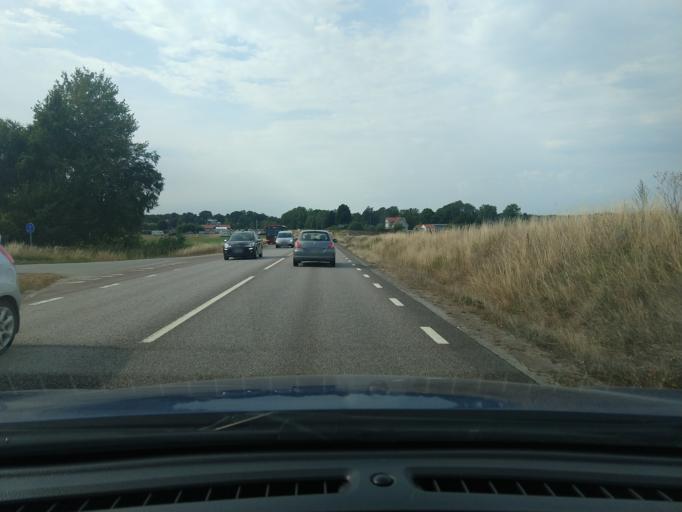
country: SE
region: Blekinge
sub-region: Karlskrona Kommun
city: Sturko
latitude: 56.1933
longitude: 15.7002
